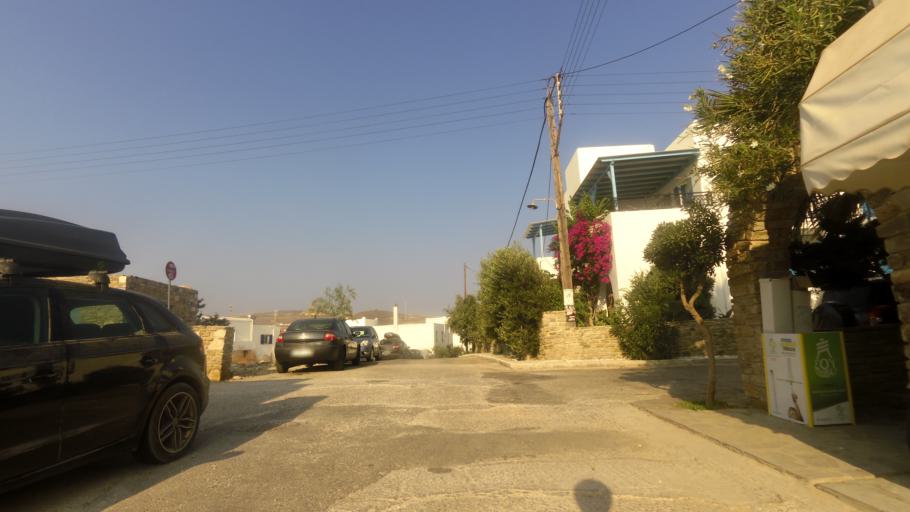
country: GR
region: South Aegean
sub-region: Nomos Kykladon
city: Antiparos
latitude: 37.0412
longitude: 25.0820
